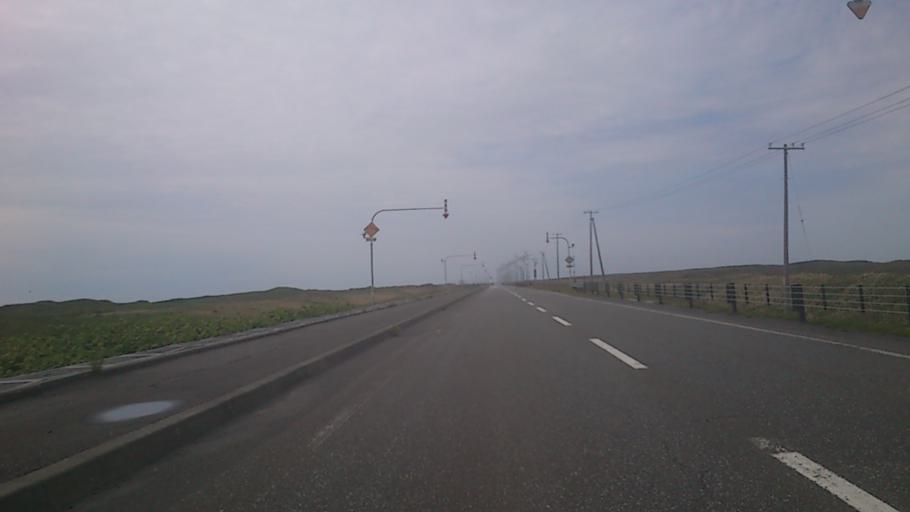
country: JP
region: Hokkaido
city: Makubetsu
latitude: 44.9379
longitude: 141.7168
